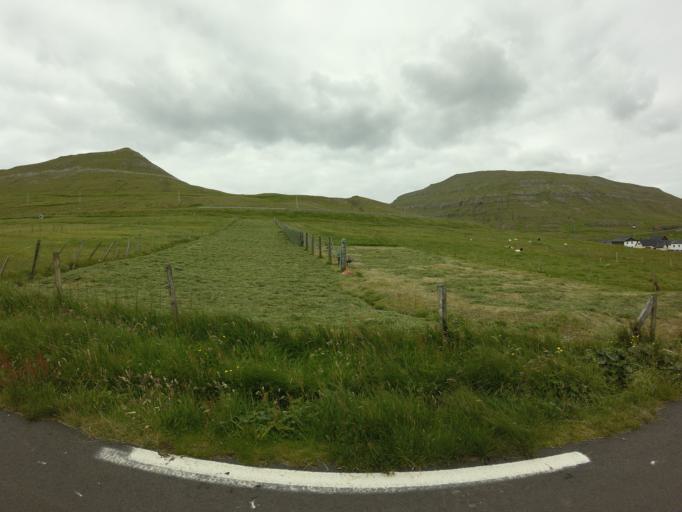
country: FO
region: Suduroy
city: Vagur
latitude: 61.4417
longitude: -6.7712
